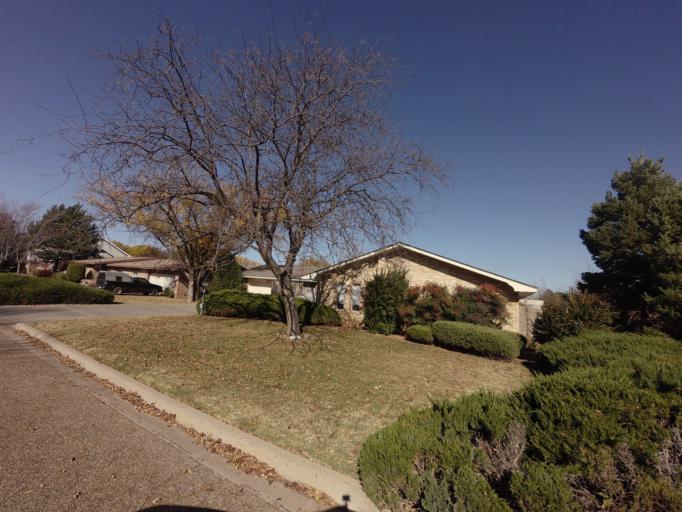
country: US
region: New Mexico
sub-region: Curry County
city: Clovis
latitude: 34.4165
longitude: -103.1809
